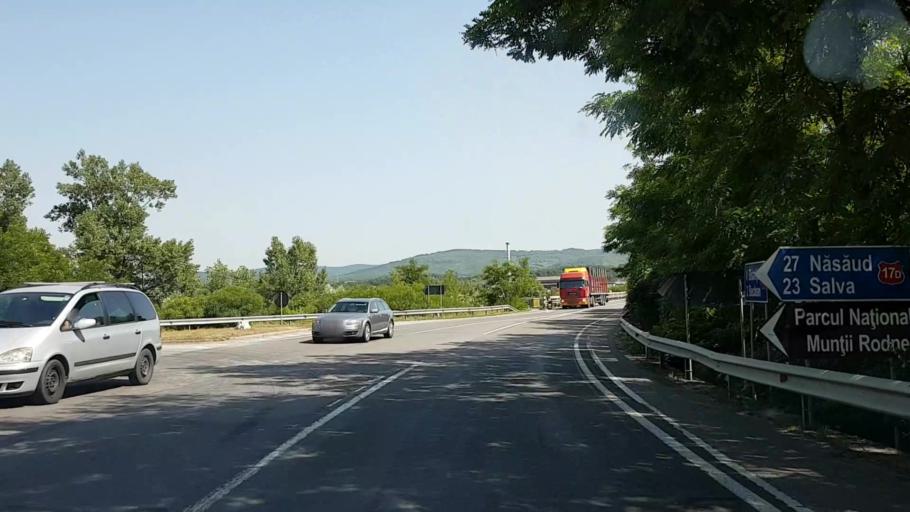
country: RO
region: Bistrita-Nasaud
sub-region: Comuna Beclean
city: Beclean
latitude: 47.1783
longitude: 24.1468
